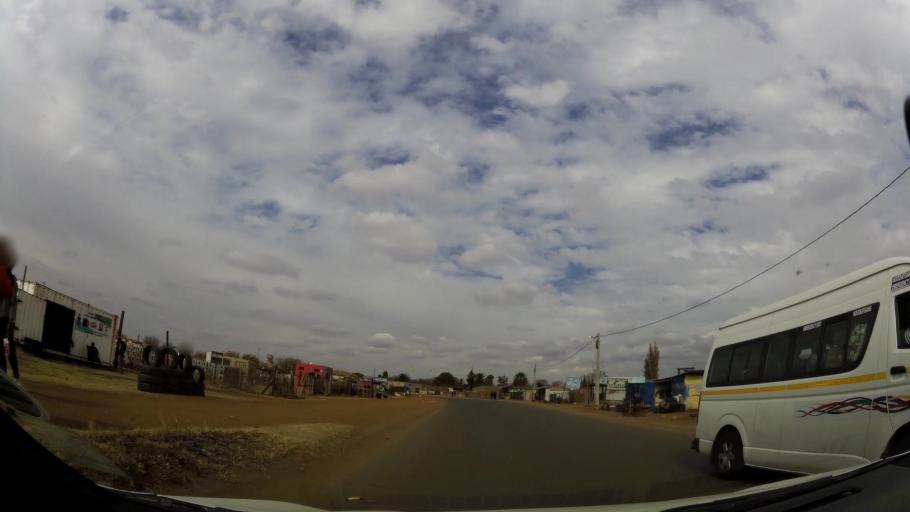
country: ZA
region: Gauteng
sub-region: Ekurhuleni Metropolitan Municipality
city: Germiston
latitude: -26.3872
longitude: 28.1382
